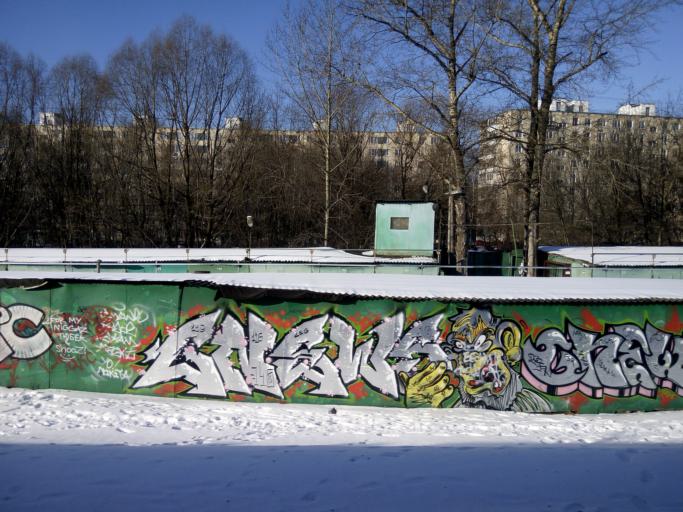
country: RU
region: Moscow
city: Slobodka
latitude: 55.8620
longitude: 37.5743
